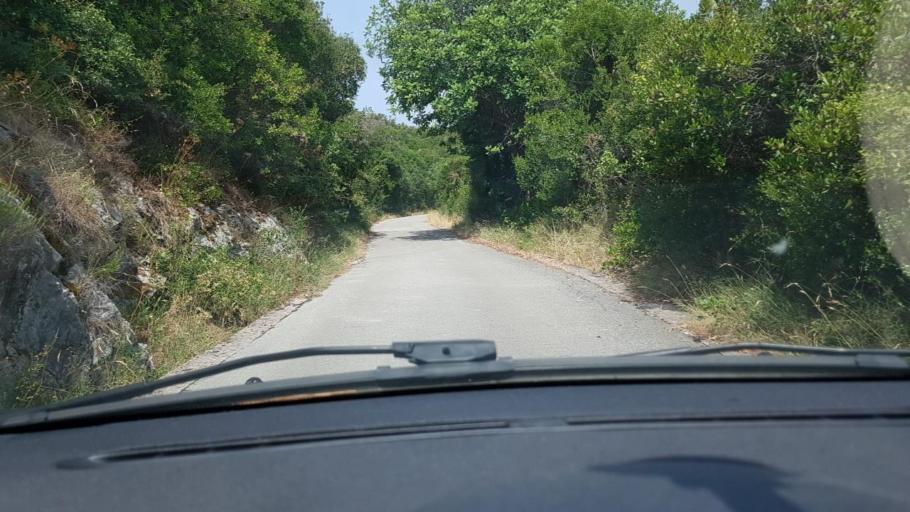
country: ME
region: Herceg Novi
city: Herceg-Novi
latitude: 42.3987
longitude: 18.5219
